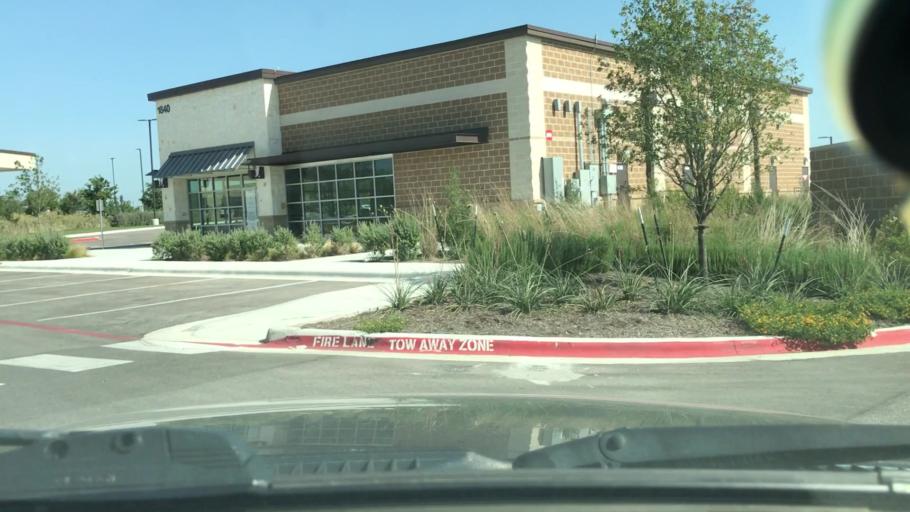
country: US
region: Texas
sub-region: Williamson County
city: Leander
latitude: 30.5449
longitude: -97.8663
